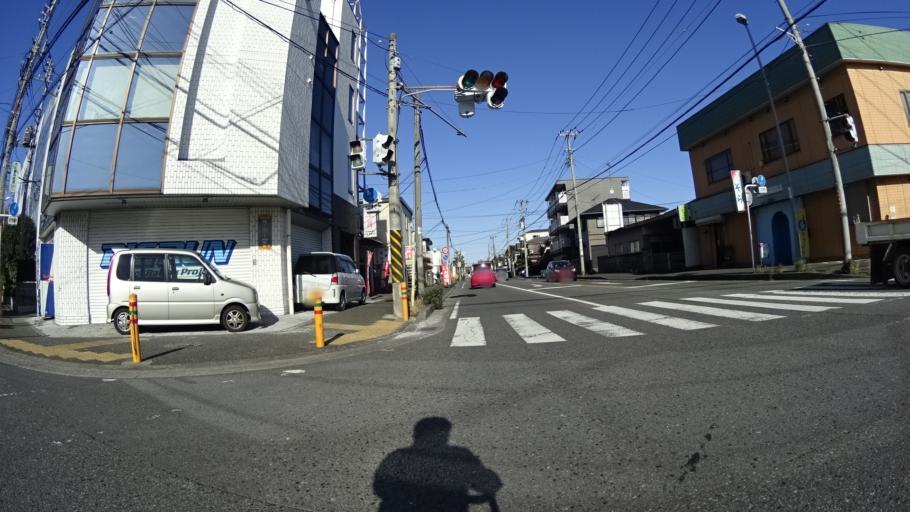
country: JP
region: Tokyo
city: Hachioji
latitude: 35.5824
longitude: 139.3618
